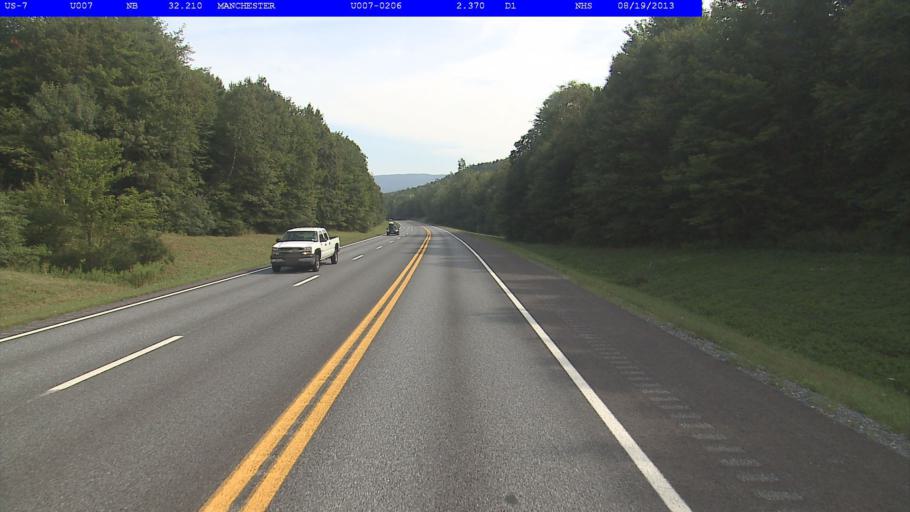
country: US
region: Vermont
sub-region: Bennington County
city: Manchester Center
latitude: 43.1447
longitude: -73.0517
